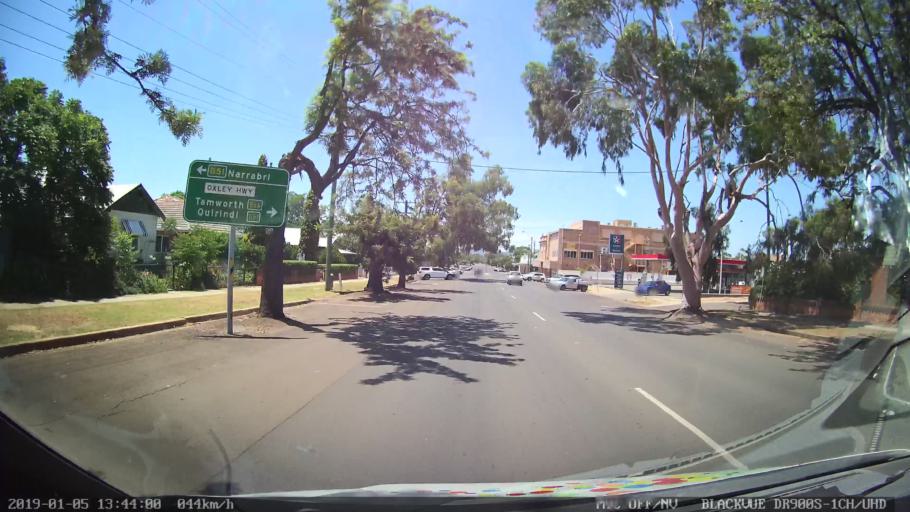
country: AU
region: New South Wales
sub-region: Gunnedah
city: Gunnedah
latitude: -30.9804
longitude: 150.2555
